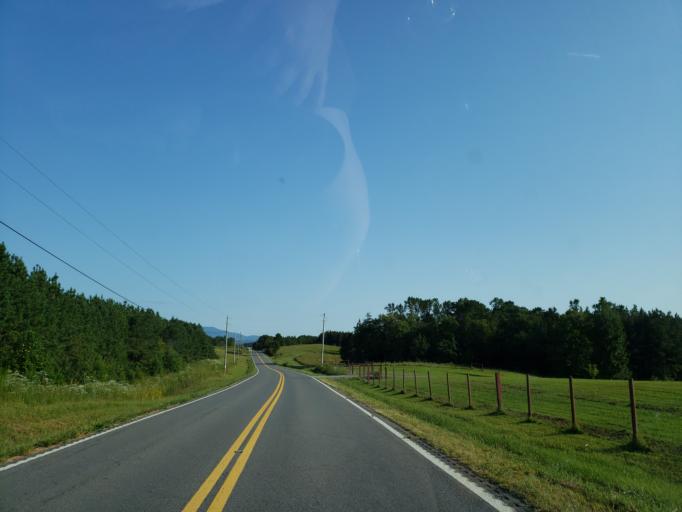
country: US
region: Tennessee
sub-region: Bradley County
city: Wildwood Lake
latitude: 35.0240
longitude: -84.7960
